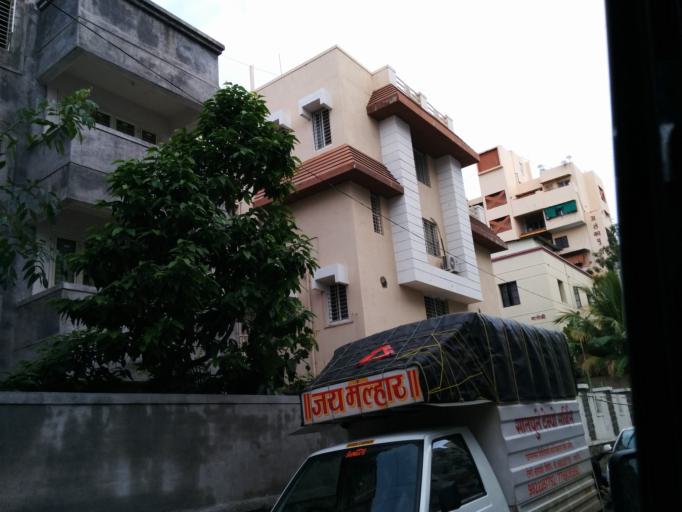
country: IN
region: Maharashtra
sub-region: Pune Division
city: Pune
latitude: 18.5132
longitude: 73.8154
